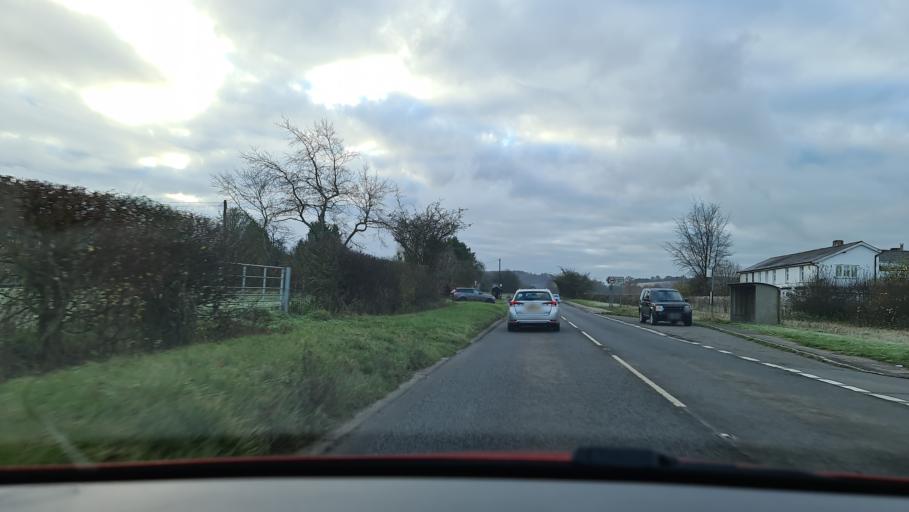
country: GB
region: England
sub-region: Buckinghamshire
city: Princes Risborough
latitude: 51.6899
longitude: -0.8322
